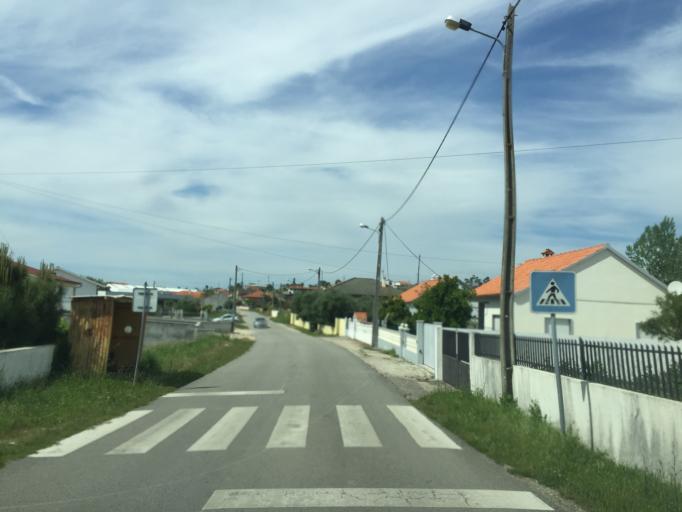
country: PT
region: Coimbra
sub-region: Soure
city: Soure
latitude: 40.0098
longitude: -8.5798
